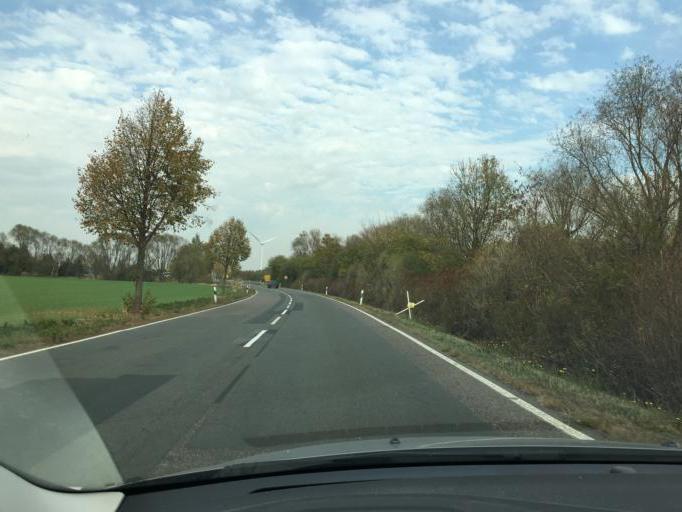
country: DE
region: Saxony
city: Zwochau
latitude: 51.4939
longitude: 12.2796
